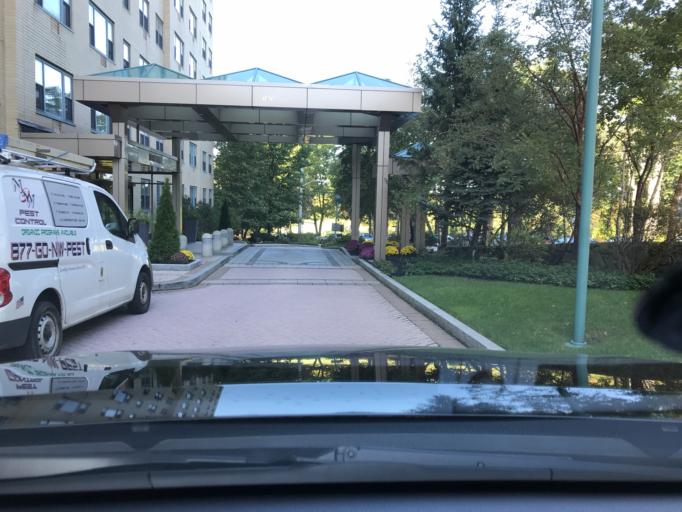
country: US
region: Massachusetts
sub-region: Middlesex County
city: Belmont
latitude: 42.3808
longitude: -71.1543
